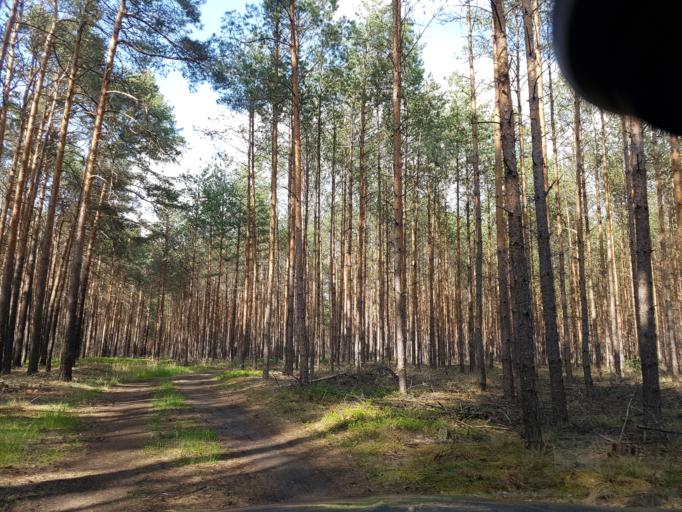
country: DE
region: Brandenburg
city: Schonewalde
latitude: 51.6369
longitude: 13.6367
